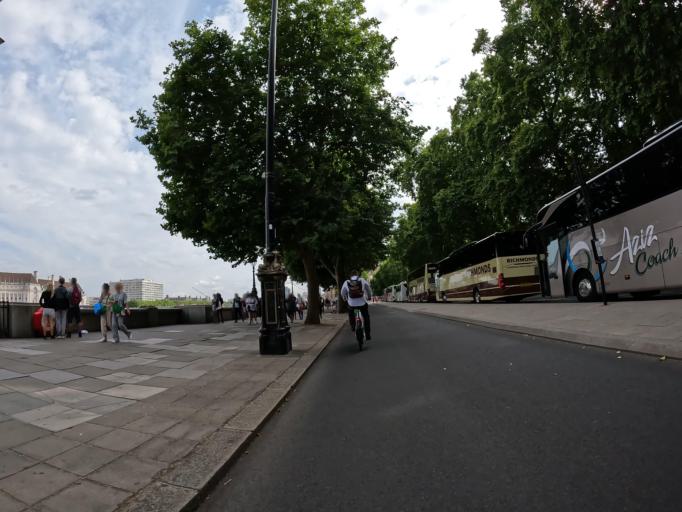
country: GB
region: England
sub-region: Greater London
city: Bromley
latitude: 51.4262
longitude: 0.0166
